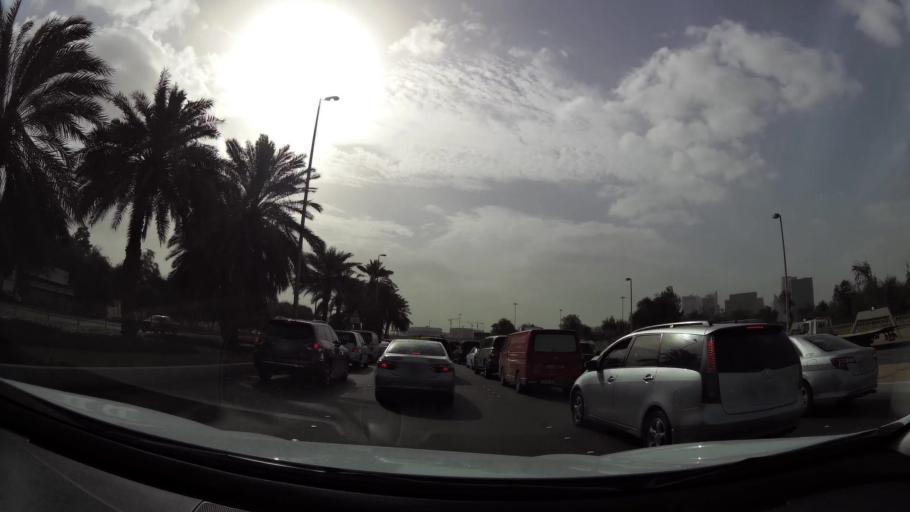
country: AE
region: Abu Dhabi
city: Abu Dhabi
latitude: 24.4291
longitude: 54.4429
